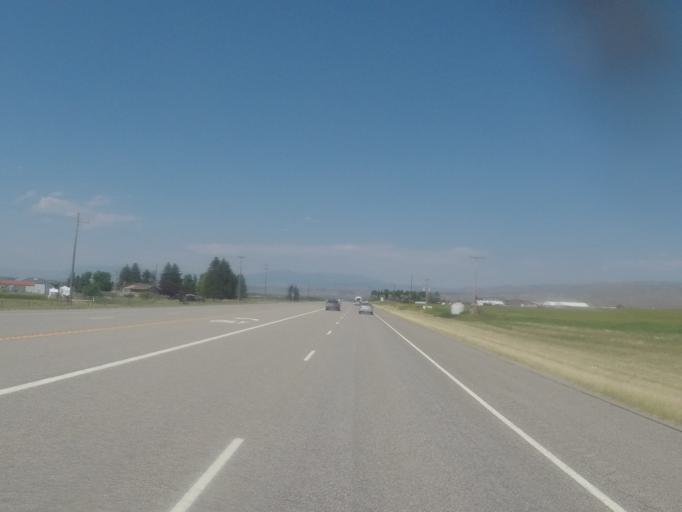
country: US
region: Montana
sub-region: Broadwater County
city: Townsend
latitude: 46.1345
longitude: -111.4832
